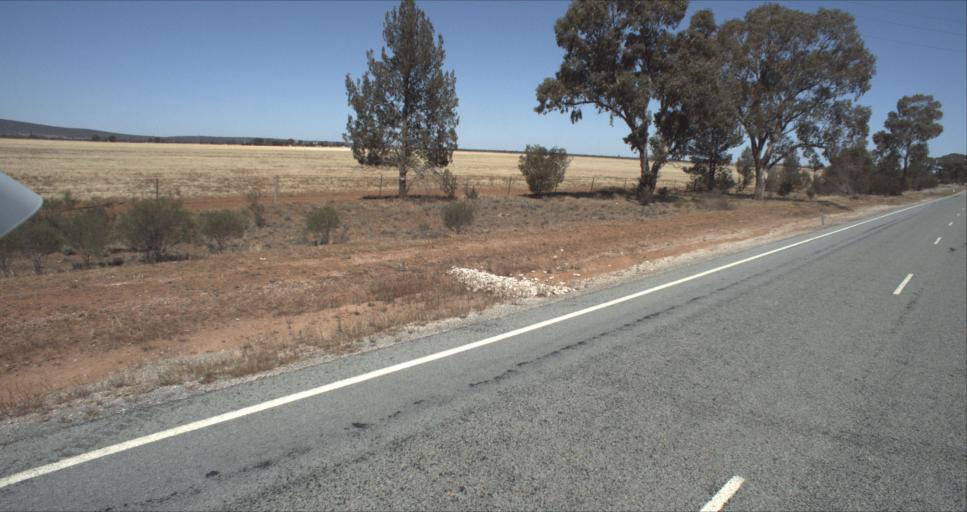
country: AU
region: New South Wales
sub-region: Leeton
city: Leeton
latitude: -34.4854
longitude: 146.4334
